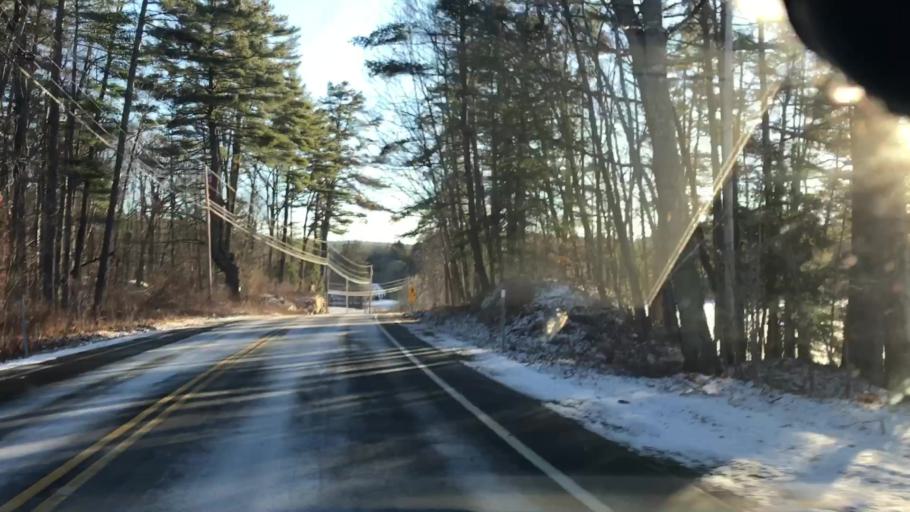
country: US
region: New Hampshire
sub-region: Grafton County
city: Lyme Town Offices
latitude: 43.8287
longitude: -72.1441
